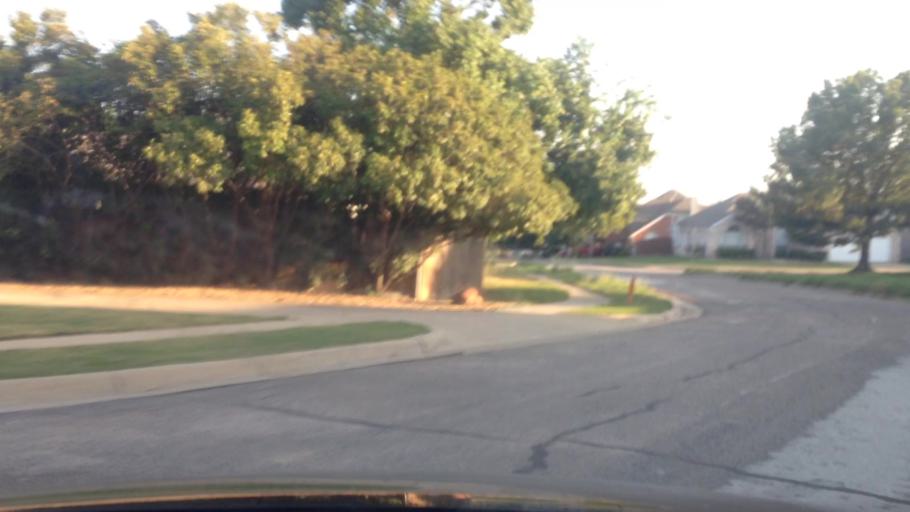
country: US
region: Texas
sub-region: Tarrant County
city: Dalworthington Gardens
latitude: 32.6526
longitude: -97.0984
